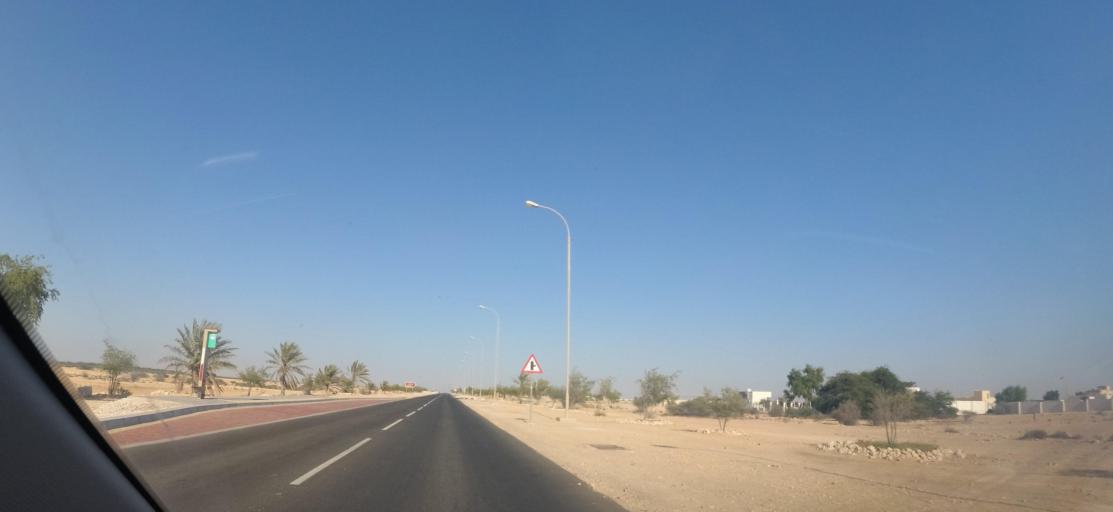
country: QA
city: Al Ghuwayriyah
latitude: 25.8321
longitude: 51.2520
